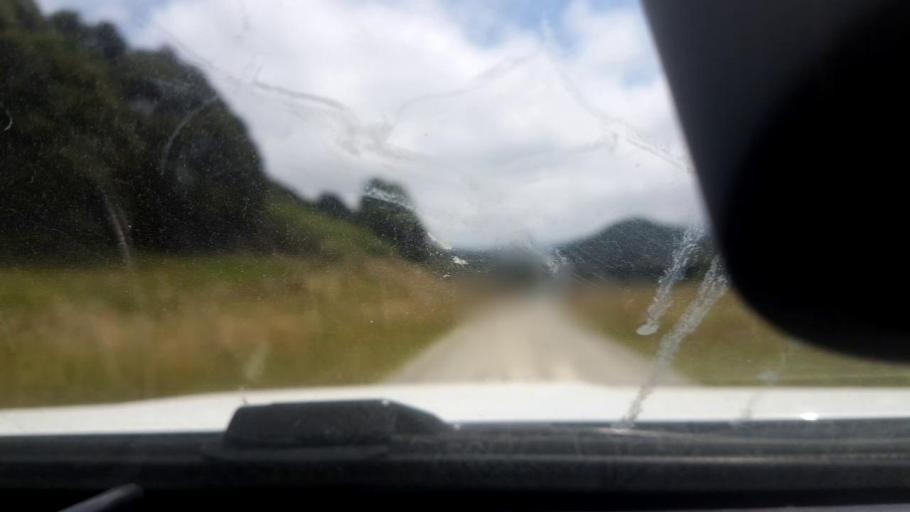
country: NZ
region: Canterbury
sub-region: Timaru District
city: Pleasant Point
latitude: -44.1512
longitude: 171.0903
